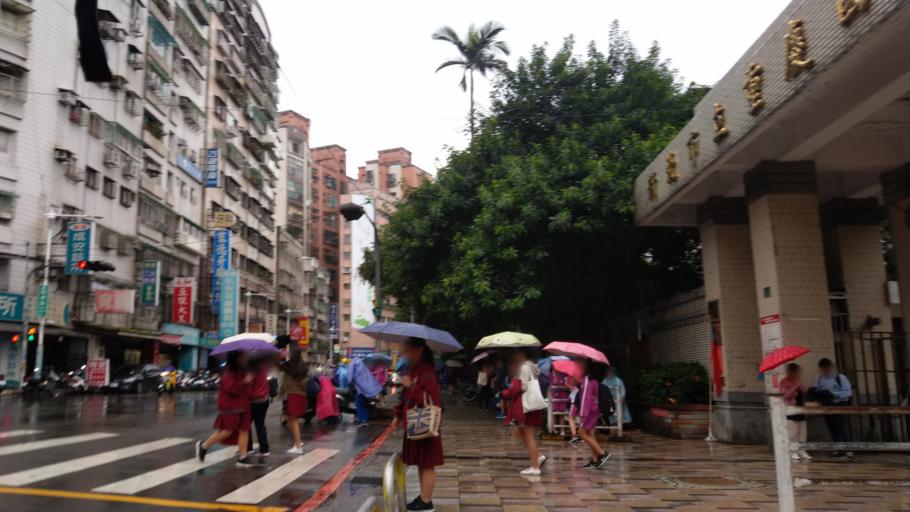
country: TW
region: Taipei
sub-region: Taipei
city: Banqiao
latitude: 24.9983
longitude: 121.4633
